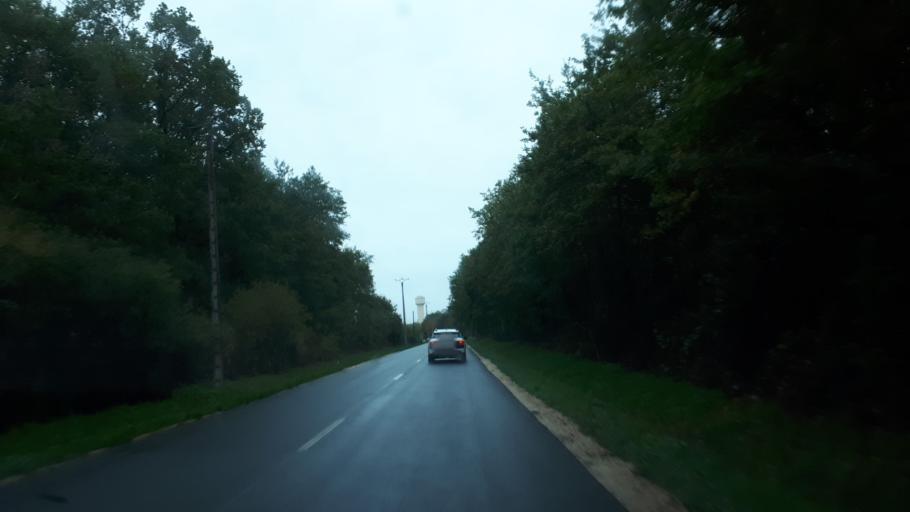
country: FR
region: Centre
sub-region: Departement du Loir-et-Cher
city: Gievres
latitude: 47.2925
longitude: 1.6709
